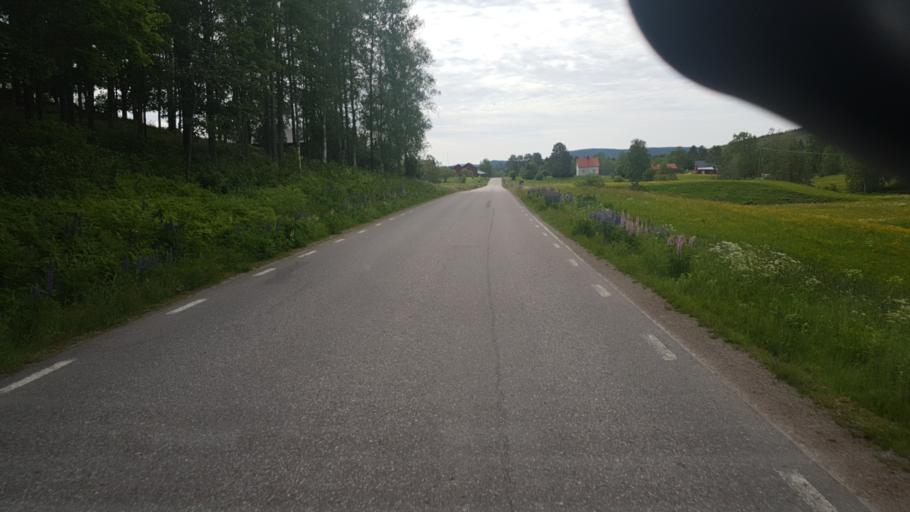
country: SE
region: Vaermland
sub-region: Arvika Kommun
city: Arvika
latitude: 59.7567
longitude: 12.7978
